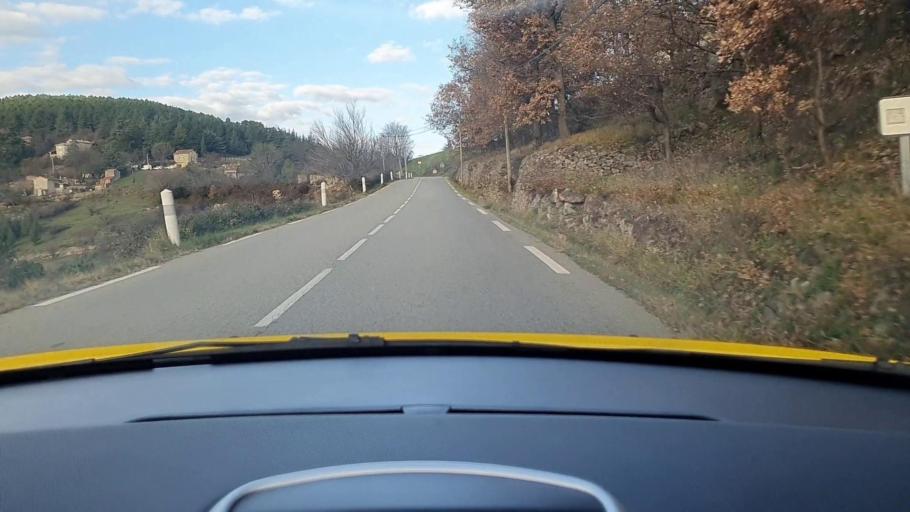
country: FR
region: Languedoc-Roussillon
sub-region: Departement du Gard
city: Branoux-les-Taillades
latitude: 44.2664
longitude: 4.0286
